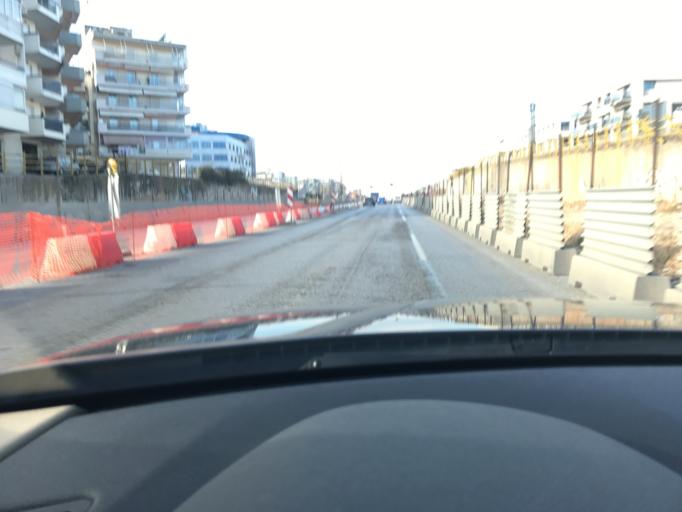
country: GR
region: Central Macedonia
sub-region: Nomos Thessalonikis
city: Stavroupoli
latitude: 40.6773
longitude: 22.9280
